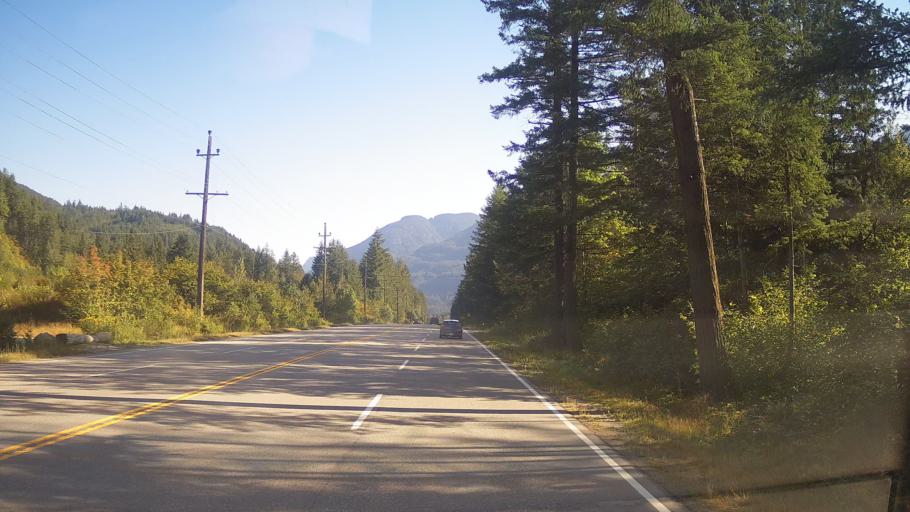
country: CA
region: British Columbia
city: Hope
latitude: 49.4682
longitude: -121.4301
